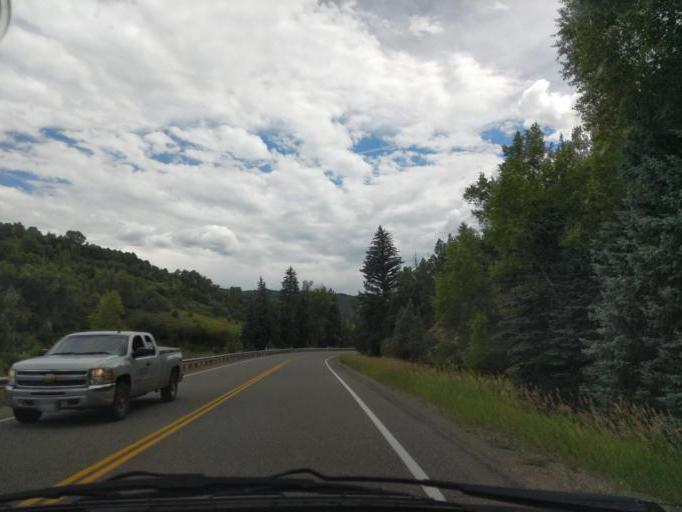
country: US
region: Colorado
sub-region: Delta County
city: Paonia
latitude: 39.0592
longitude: -107.3635
